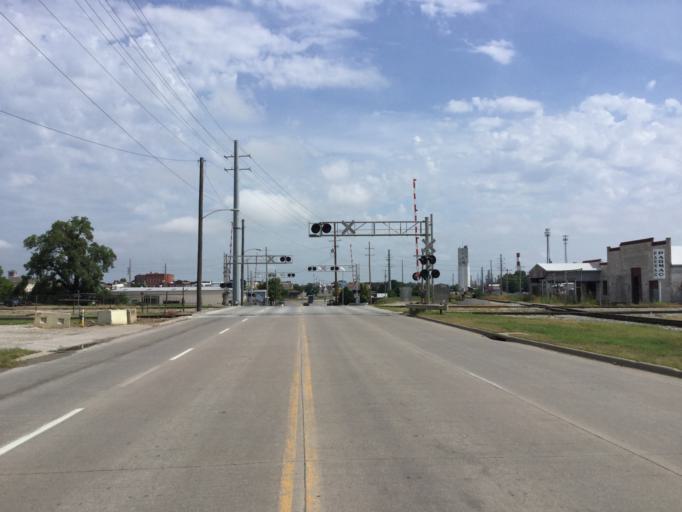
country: US
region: Kansas
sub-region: Montgomery County
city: Coffeyville
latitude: 37.0297
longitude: -95.6158
